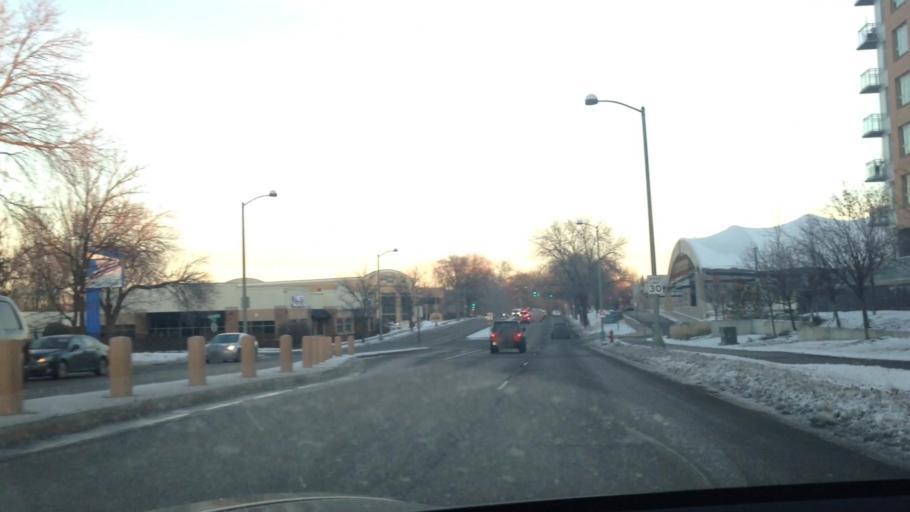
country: US
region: Minnesota
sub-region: Hennepin County
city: Saint Louis Park
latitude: 44.9379
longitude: -93.3453
